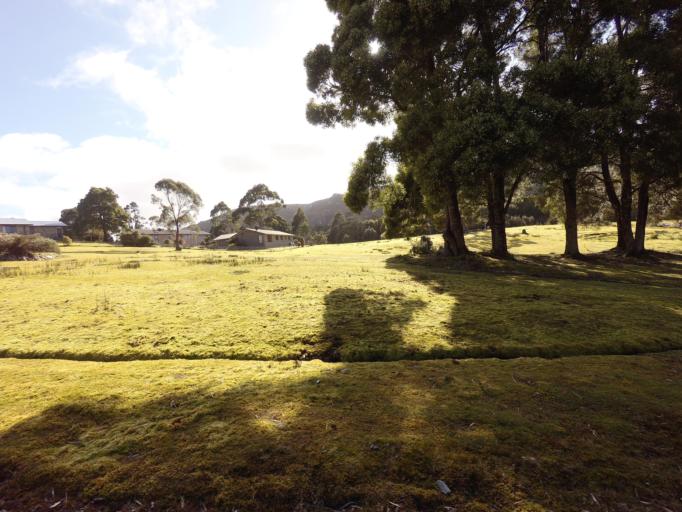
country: AU
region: Tasmania
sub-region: West Coast
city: Queenstown
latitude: -42.7682
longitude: 146.0469
